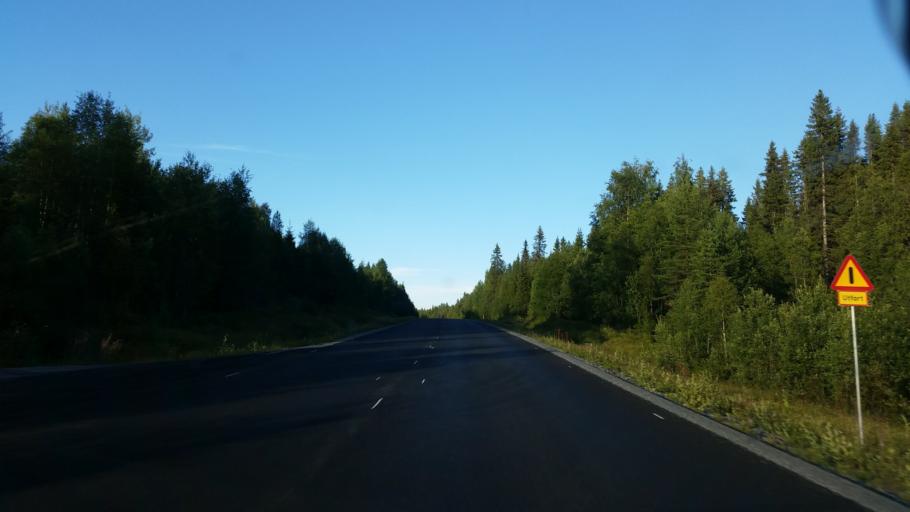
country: SE
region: Vaesterbotten
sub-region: Dorotea Kommun
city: Dorotea
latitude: 64.3010
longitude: 16.5732
